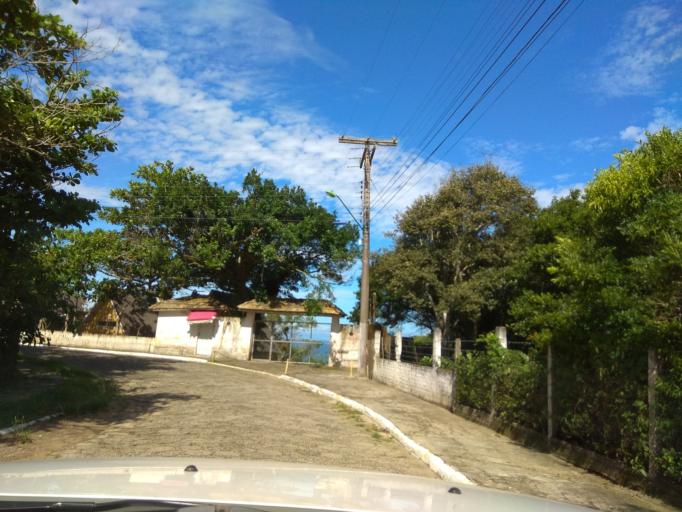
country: BR
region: Santa Catarina
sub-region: Laguna
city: Laguna
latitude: -28.4861
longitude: -48.7759
